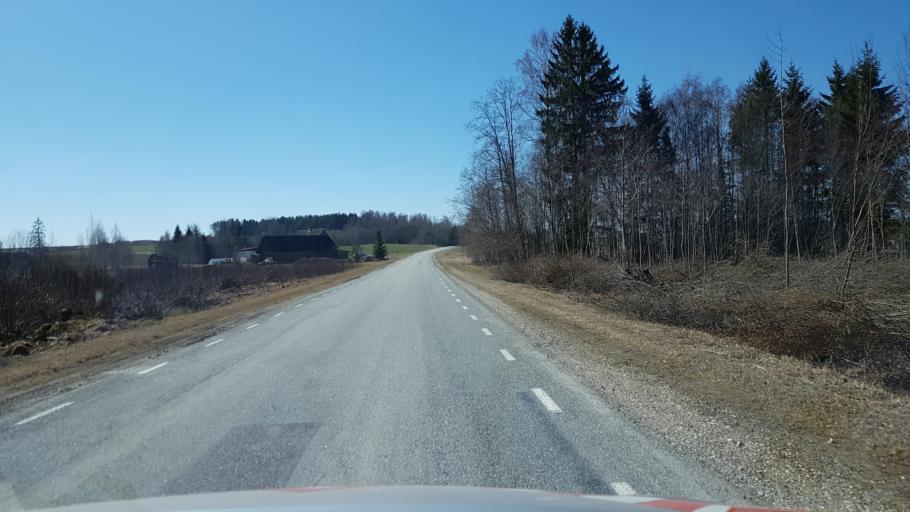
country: EE
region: Laeaene-Virumaa
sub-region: Rakke vald
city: Rakke
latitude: 59.0101
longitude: 26.3343
